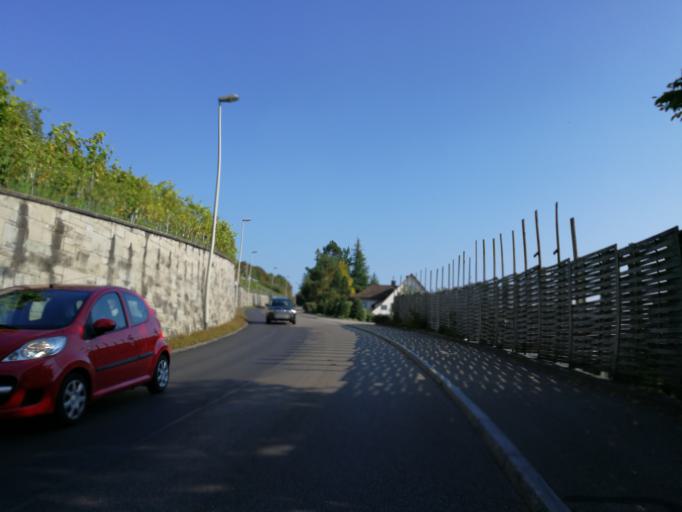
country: CH
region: Zurich
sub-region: Bezirk Meilen
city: Stafa
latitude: 47.2480
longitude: 8.7272
